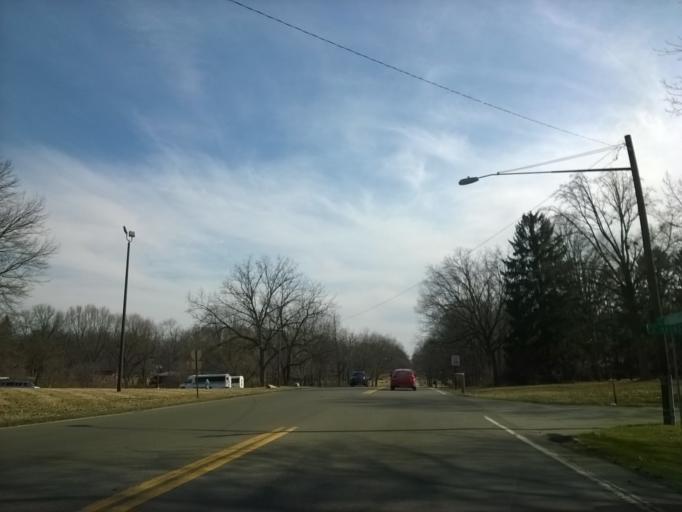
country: US
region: Indiana
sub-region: Marion County
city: Speedway
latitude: 39.8202
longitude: -86.2113
